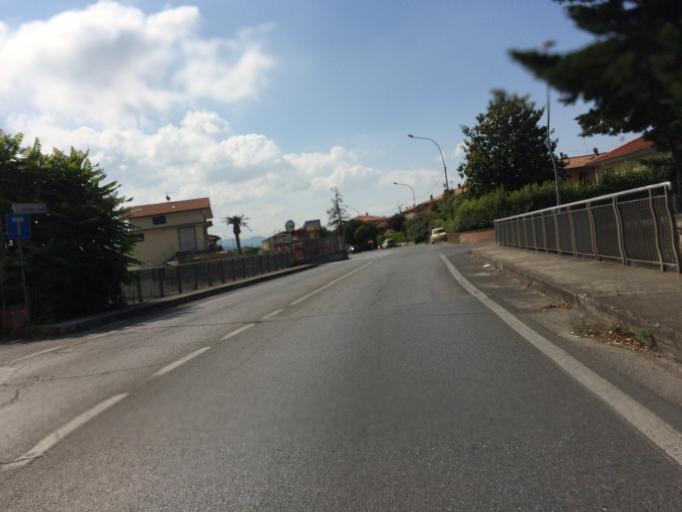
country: IT
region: Tuscany
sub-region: Provincia di Lucca
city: Ripa-Pozzi-Querceta-Ponterosso
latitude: 43.9690
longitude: 10.2104
